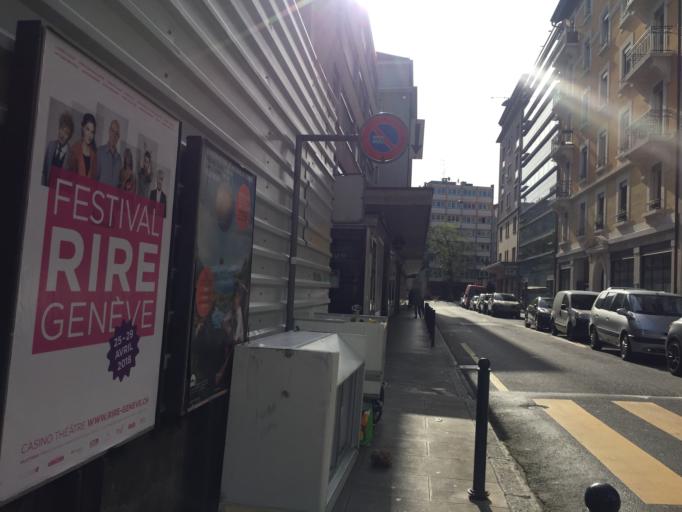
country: CH
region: Geneva
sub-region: Geneva
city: Geneve
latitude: 46.2120
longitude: 6.1484
